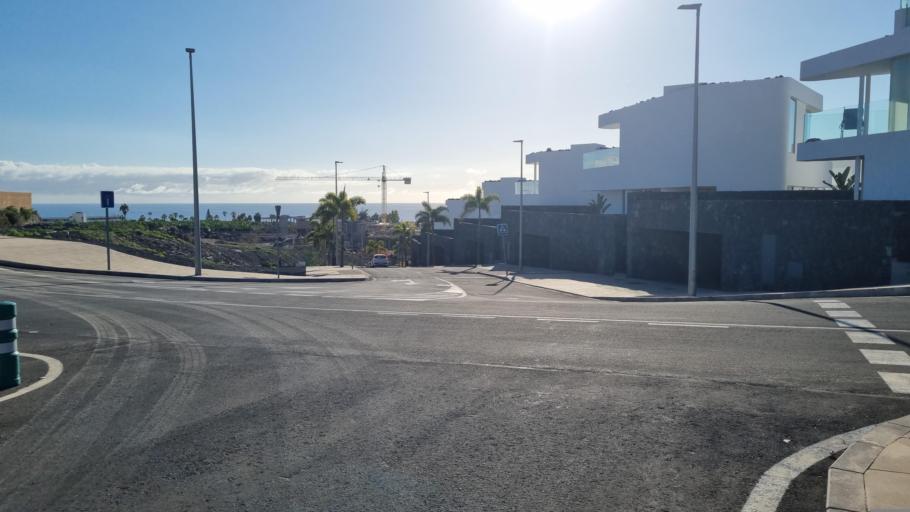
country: ES
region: Canary Islands
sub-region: Provincia de Santa Cruz de Tenerife
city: Adeje
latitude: 28.1352
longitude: -16.7823
